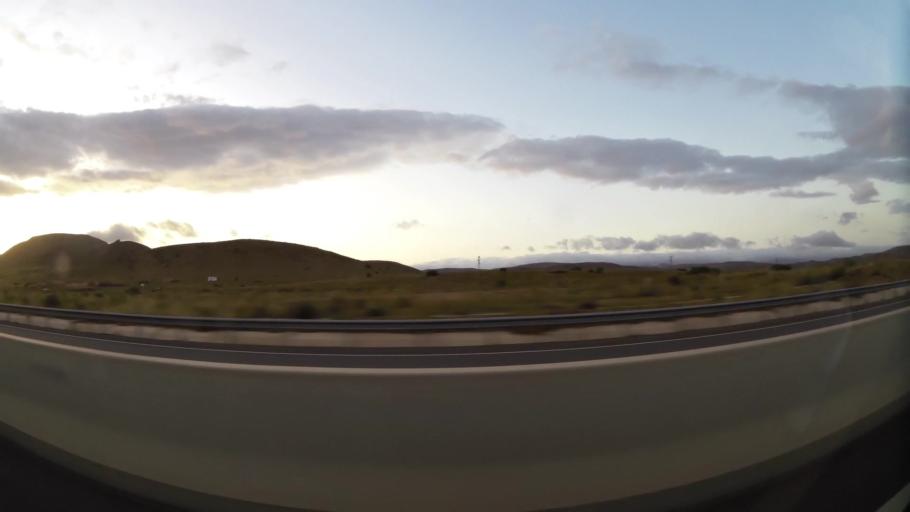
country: MA
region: Oriental
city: El Aioun
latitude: 34.6044
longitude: -2.6173
